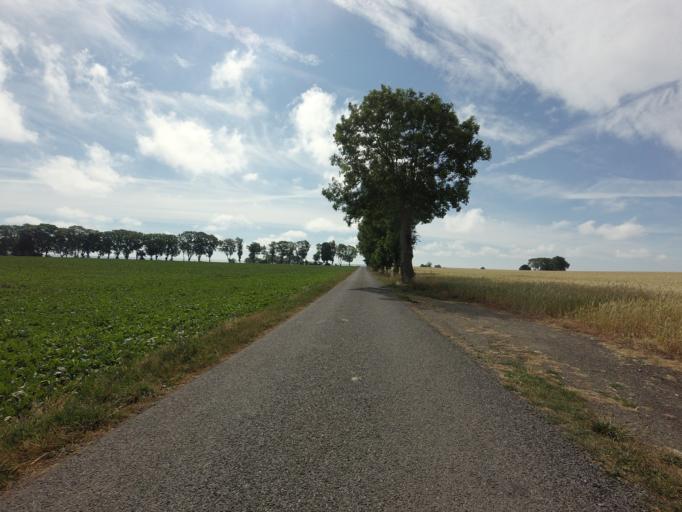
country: SE
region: Skane
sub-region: Simrishamns Kommun
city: Simrishamn
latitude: 55.4904
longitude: 14.3091
